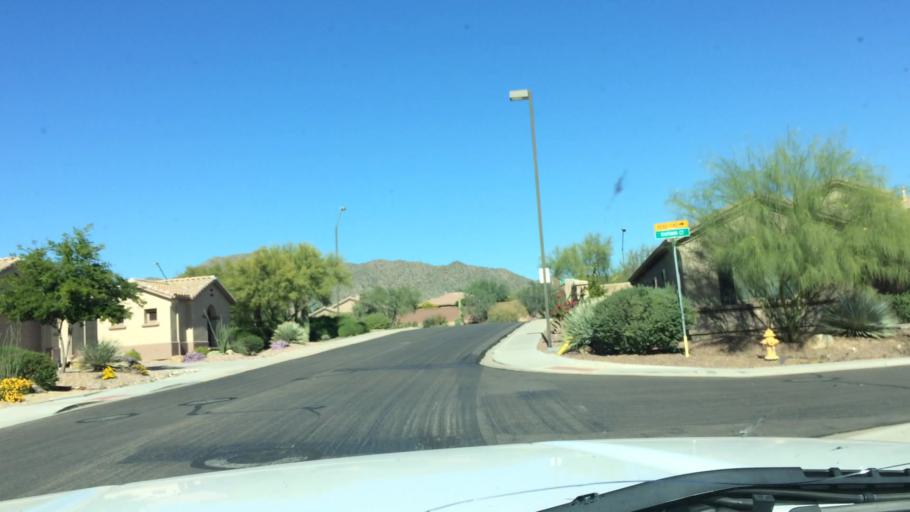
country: US
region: Arizona
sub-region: Maricopa County
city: Anthem
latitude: 33.8574
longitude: -112.1089
